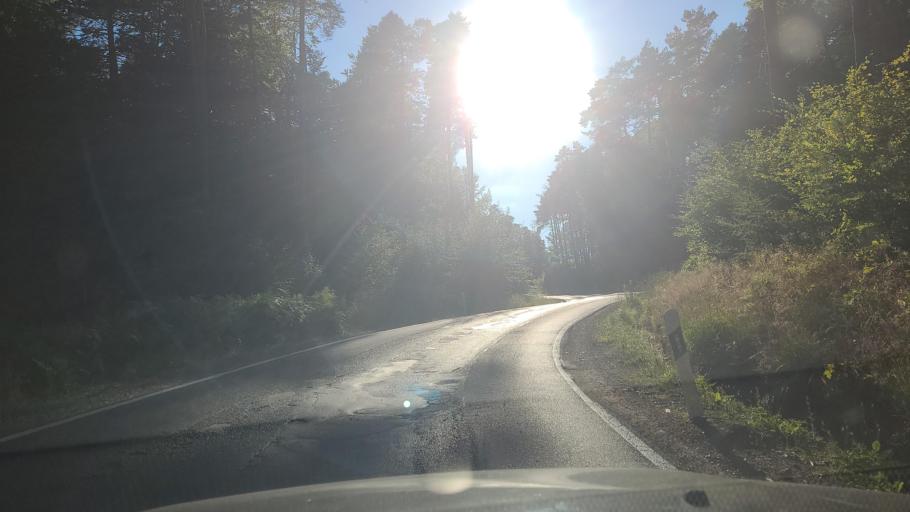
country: DE
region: Rheinland-Pfalz
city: Dierscheid
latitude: 49.9050
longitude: 6.7330
